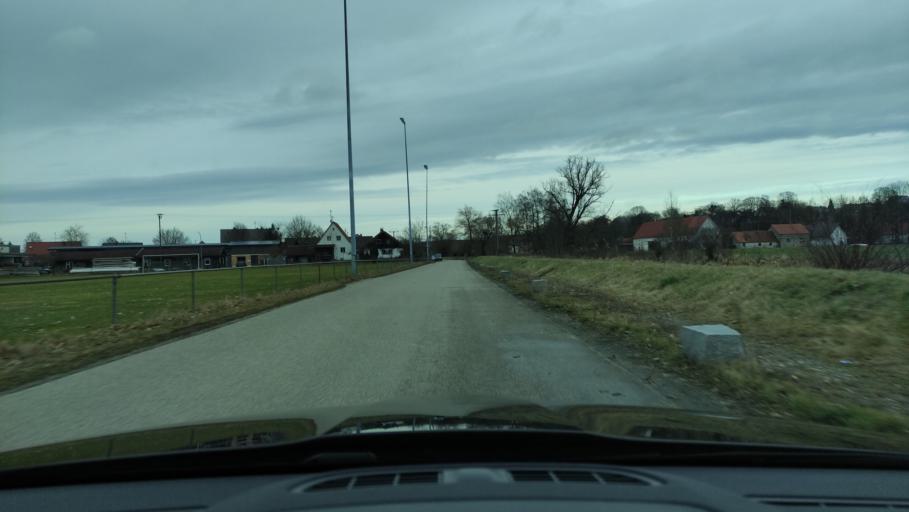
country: DE
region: Bavaria
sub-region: Swabia
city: Deisenhausen
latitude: 48.2559
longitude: 10.3200
